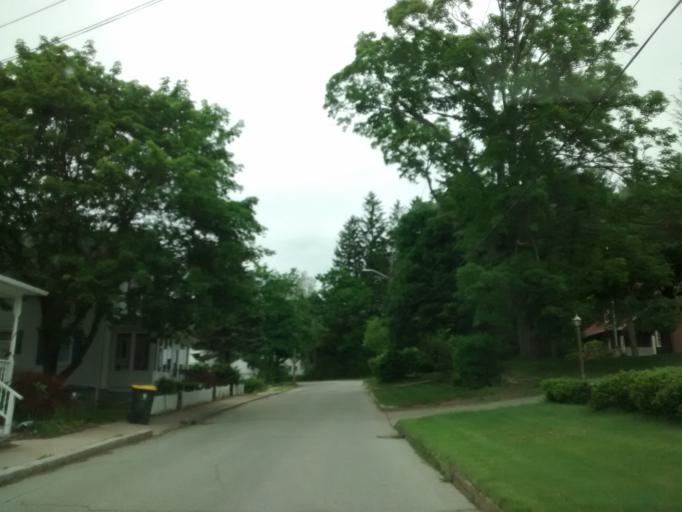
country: US
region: Rhode Island
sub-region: Providence County
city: Harrisville
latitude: 41.9662
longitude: -71.6719
